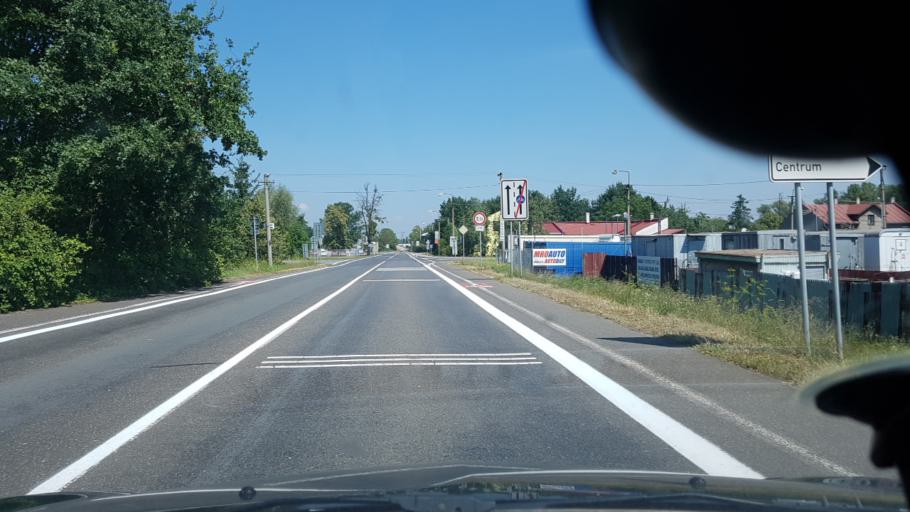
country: CZ
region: Moravskoslezsky
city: Stary Bohumin
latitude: 49.9066
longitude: 18.3369
